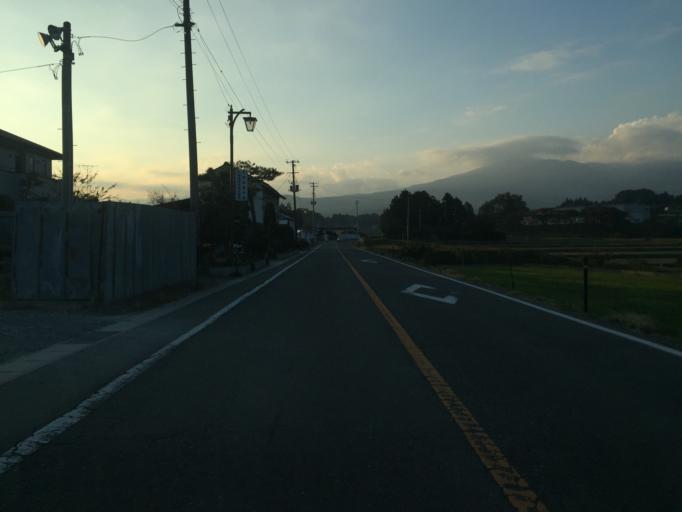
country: JP
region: Fukushima
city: Motomiya
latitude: 37.5445
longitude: 140.3721
